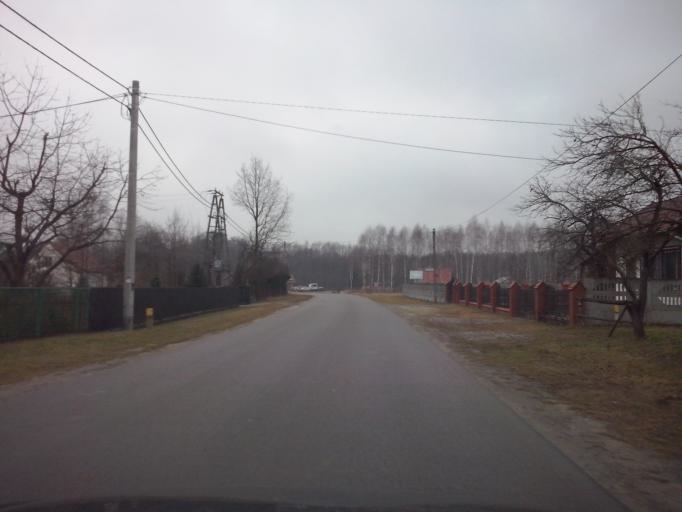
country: PL
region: Subcarpathian Voivodeship
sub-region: Powiat nizanski
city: Bieliny
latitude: 50.4262
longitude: 22.3174
